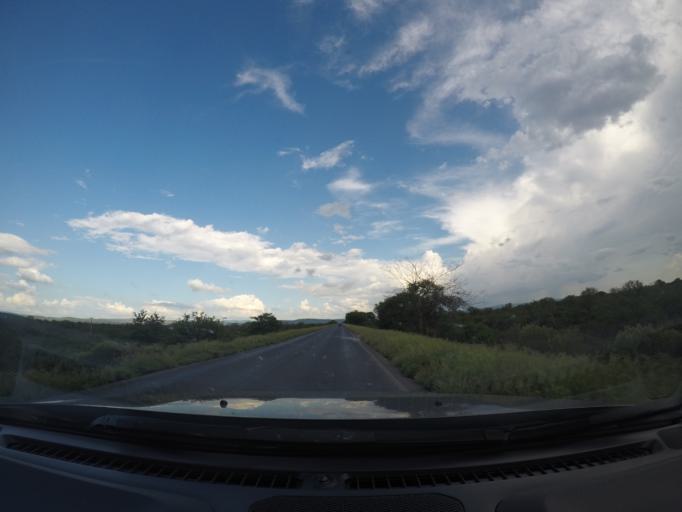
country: BR
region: Bahia
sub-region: Ibotirama
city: Ibotirama
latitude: -12.1642
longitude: -43.2819
